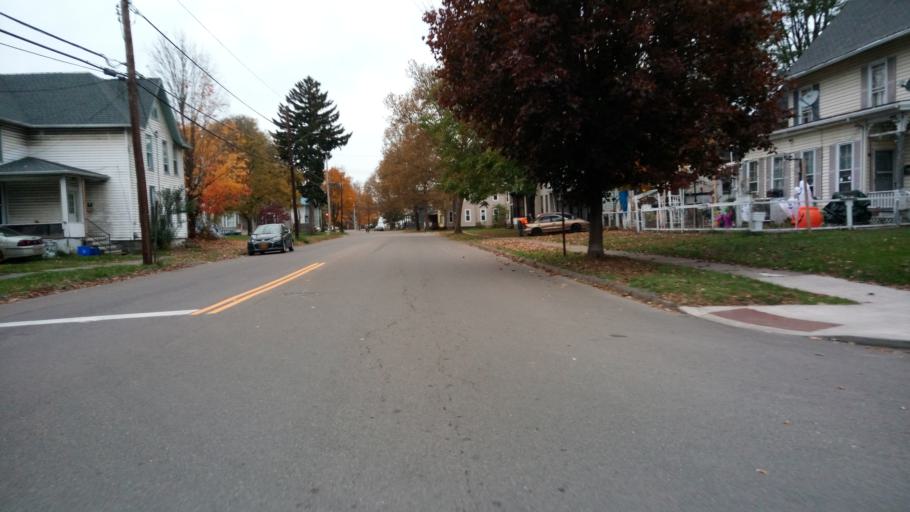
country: US
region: New York
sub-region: Chemung County
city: Elmira
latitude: 42.0827
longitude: -76.7976
